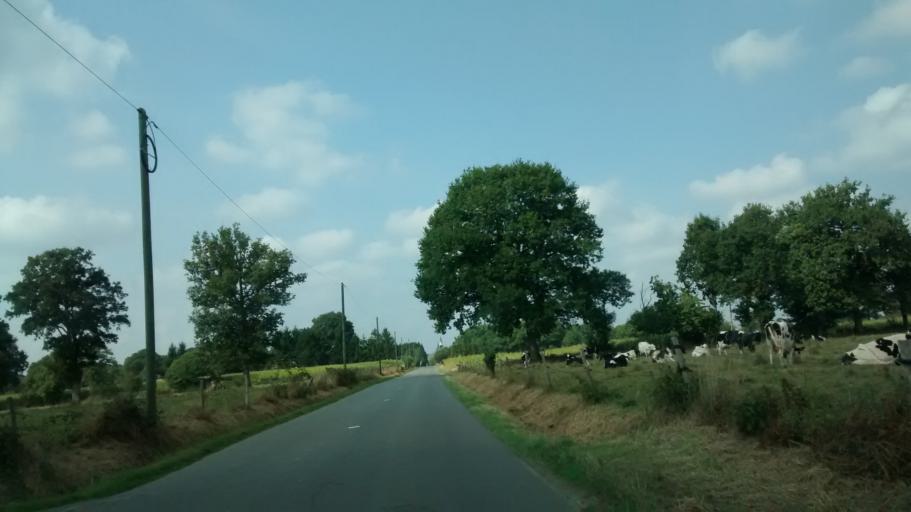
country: FR
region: Brittany
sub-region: Departement d'Ille-et-Vilaine
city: Livre-sur-Changeon
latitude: 48.2330
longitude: -1.2883
